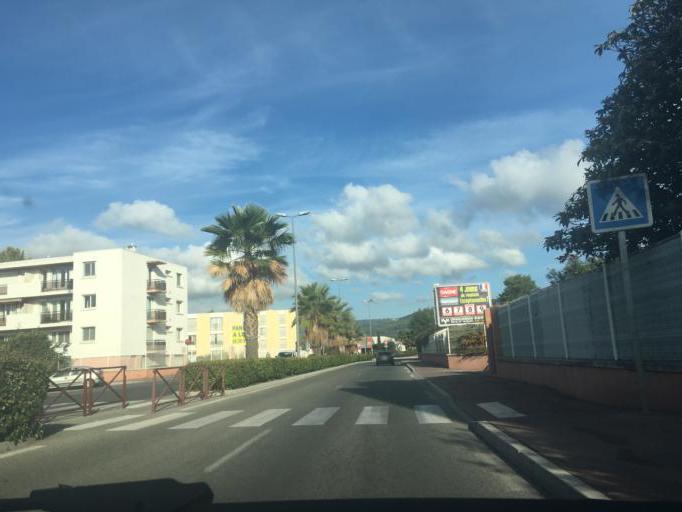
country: FR
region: Provence-Alpes-Cote d'Azur
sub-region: Departement du Var
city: Draguignan
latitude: 43.5304
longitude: 6.4663
